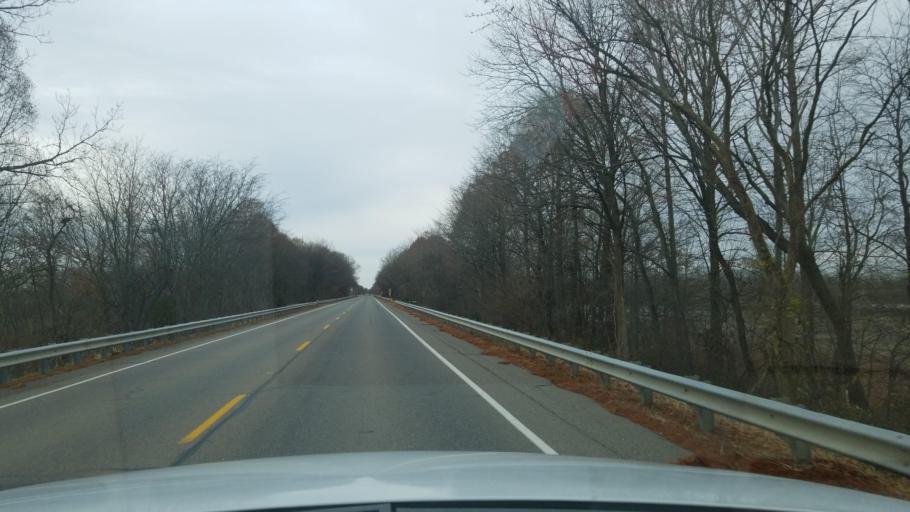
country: US
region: Indiana
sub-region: Posey County
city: Mount Vernon
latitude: 37.9290
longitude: -87.9756
